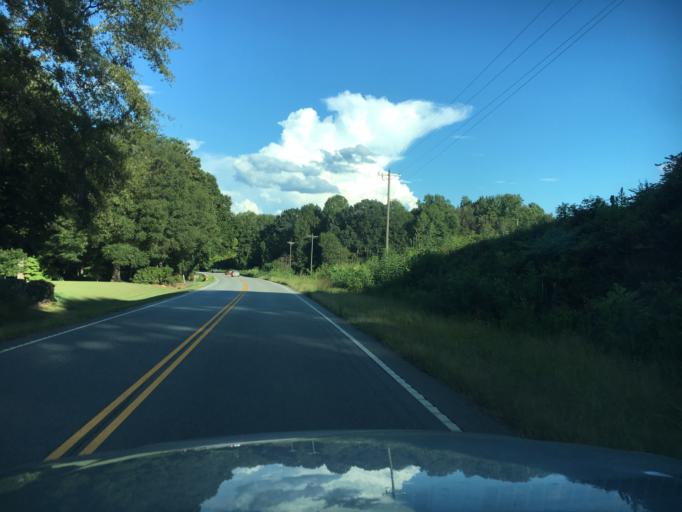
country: US
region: South Carolina
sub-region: Greenville County
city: Five Forks
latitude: 34.7937
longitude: -82.1383
